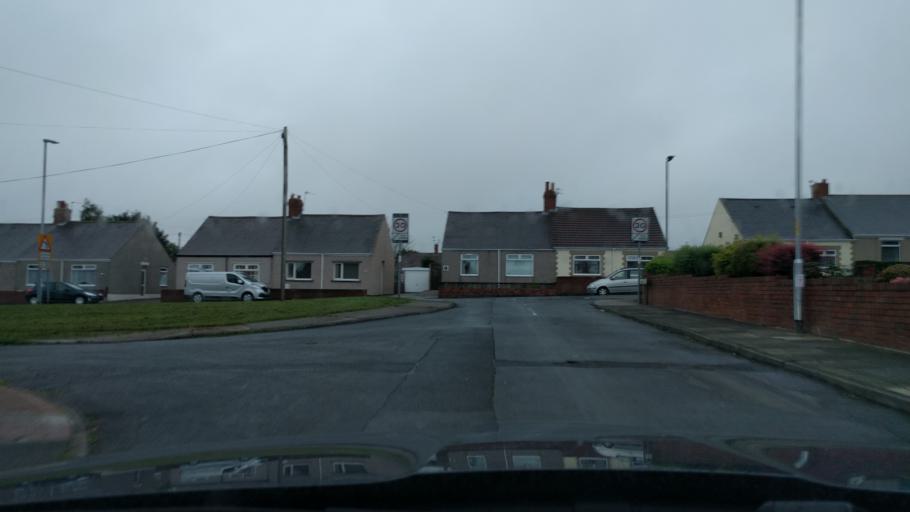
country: GB
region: England
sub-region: Northumberland
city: Bedlington
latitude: 55.1331
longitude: -1.5711
